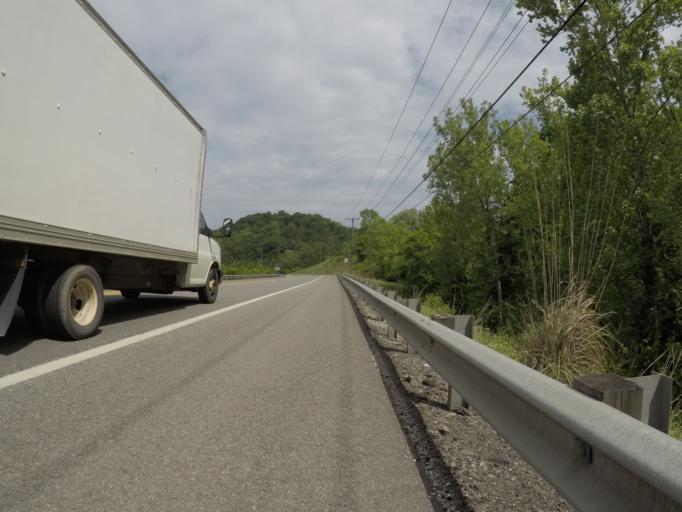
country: US
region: West Virginia
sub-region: Wayne County
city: Kenova
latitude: 38.3364
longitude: -82.5810
